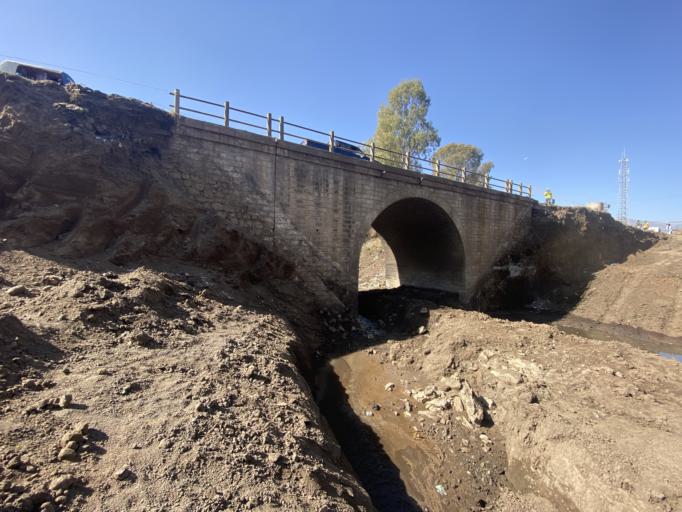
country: ET
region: Amhara
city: Robit
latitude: 11.8251
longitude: 39.5904
